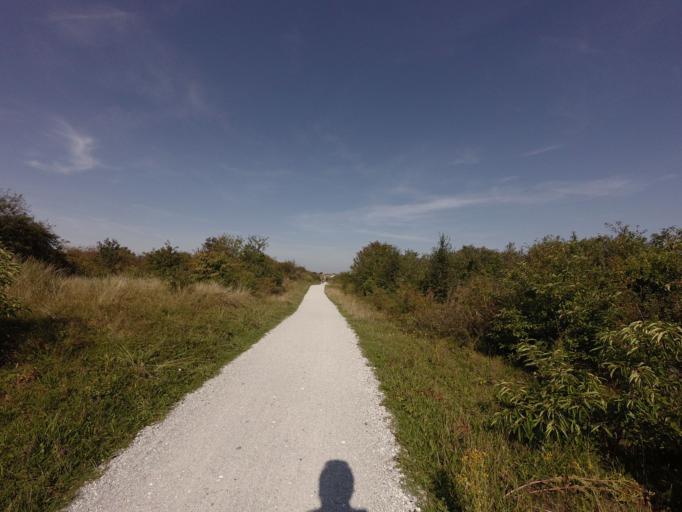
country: NL
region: Friesland
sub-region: Gemeente Schiermonnikoog
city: Schiermonnikoog
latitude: 53.4727
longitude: 6.1435
